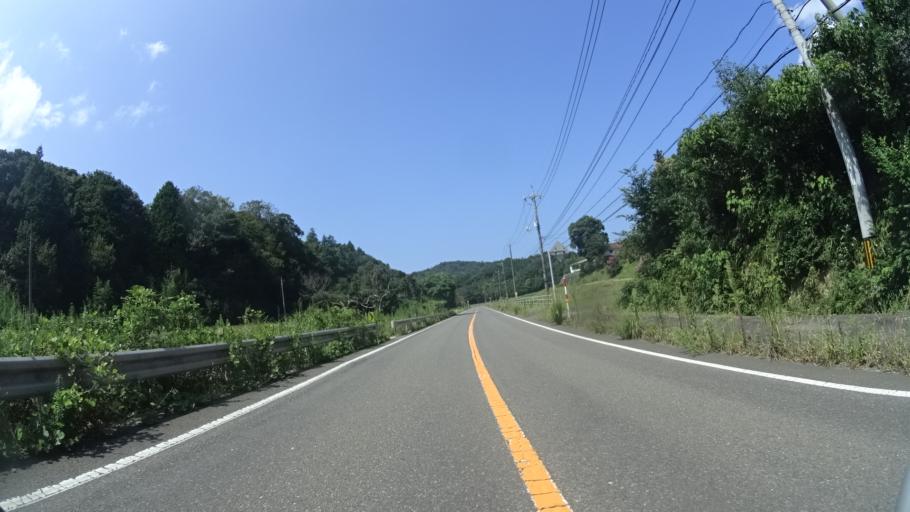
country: JP
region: Shimane
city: Masuda
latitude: 34.6258
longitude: 131.6208
